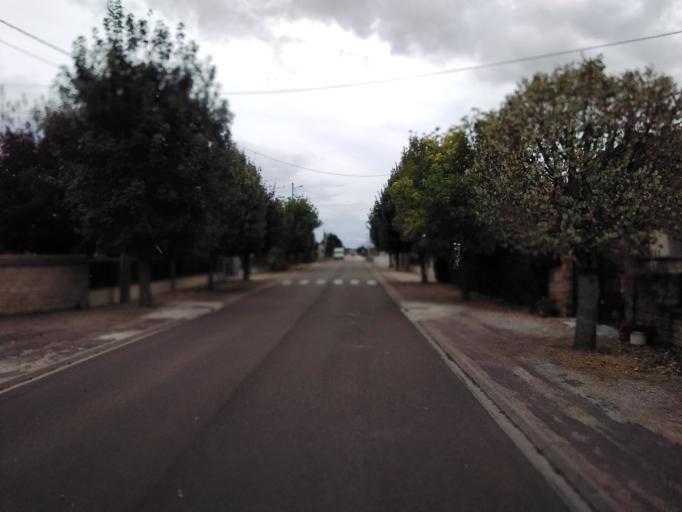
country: FR
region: Champagne-Ardenne
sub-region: Departement de l'Aube
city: Brienne-le-Chateau
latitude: 48.3861
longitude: 4.5292
